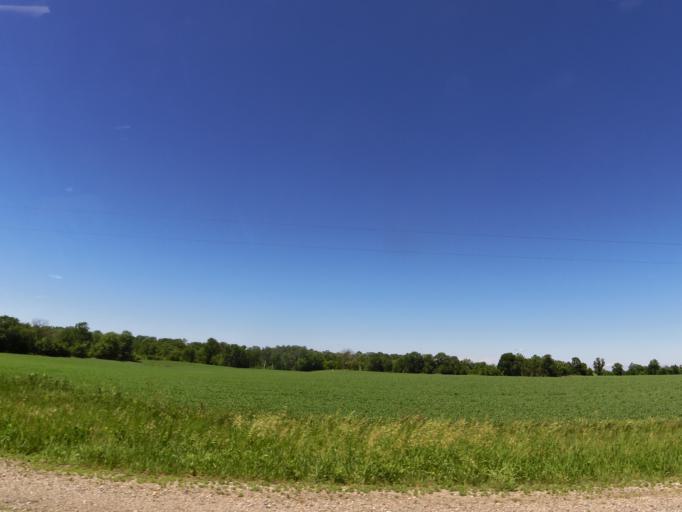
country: US
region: Minnesota
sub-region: Becker County
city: Detroit Lakes
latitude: 47.0238
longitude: -95.9124
